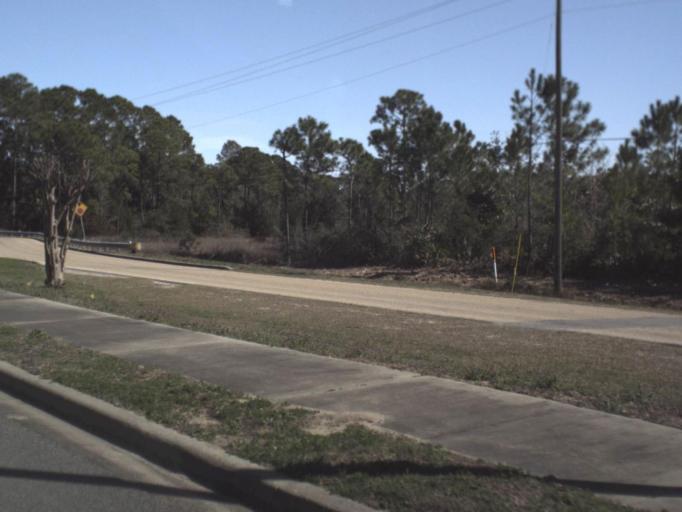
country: US
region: Florida
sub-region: Bay County
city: Lynn Haven
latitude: 30.2650
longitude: -85.6458
